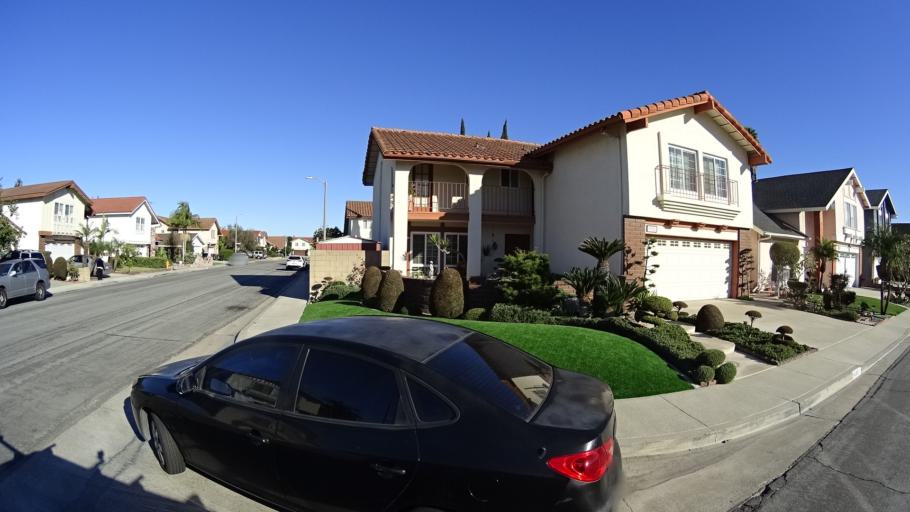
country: US
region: California
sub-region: Orange County
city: Garden Grove
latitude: 33.7686
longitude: -117.9654
